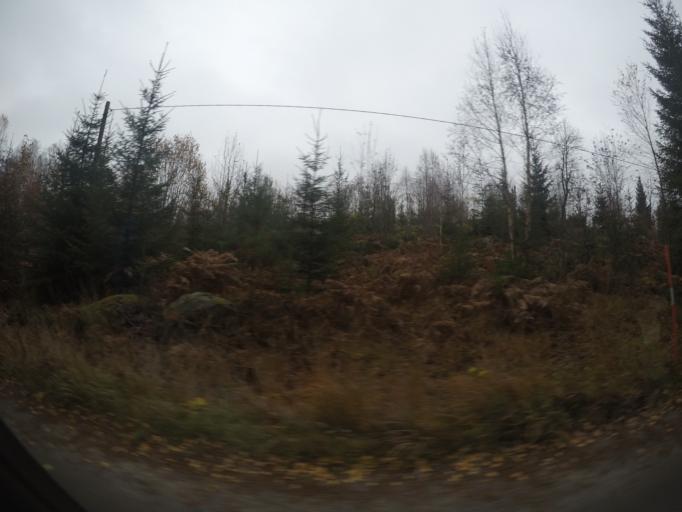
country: SE
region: Vaestmanland
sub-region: Surahammars Kommun
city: Ramnas
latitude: 59.7176
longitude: 16.0925
